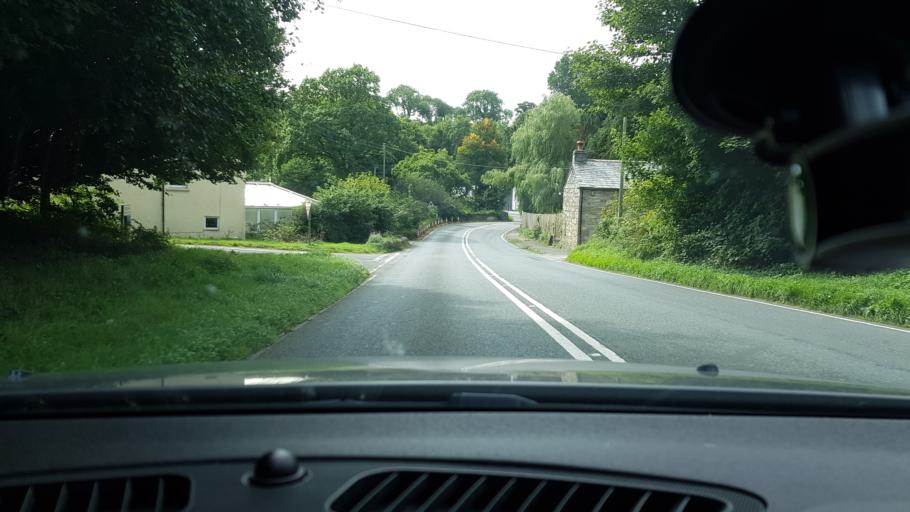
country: GB
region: England
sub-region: Cornwall
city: Camelford
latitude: 50.5937
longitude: -4.7249
